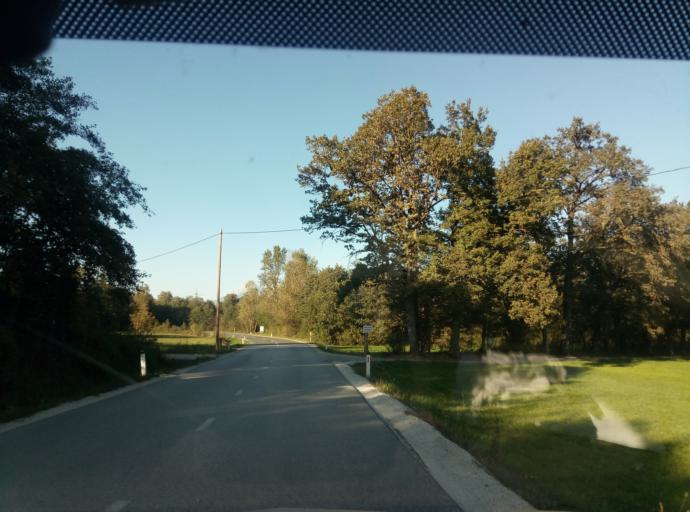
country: SI
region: Medvode
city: Zgornje Pirnice
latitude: 46.1315
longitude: 14.4777
